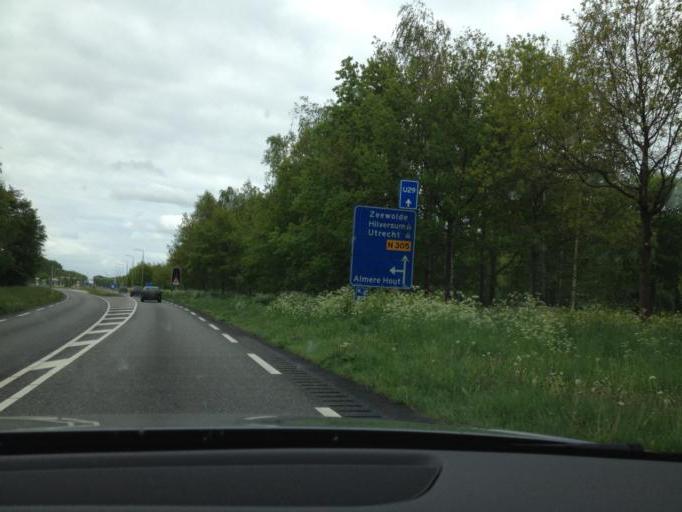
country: NL
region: North Holland
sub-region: Gemeente Huizen
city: Huizen
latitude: 52.3305
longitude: 5.2887
